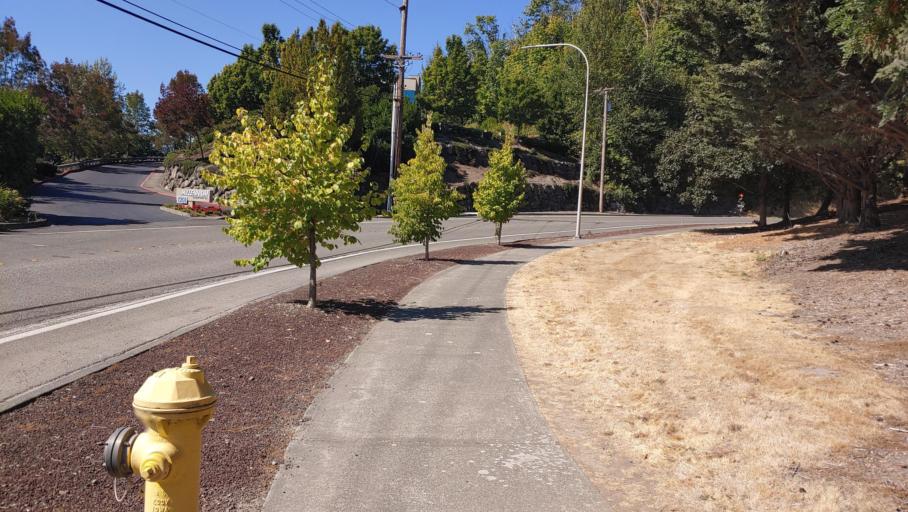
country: US
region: Washington
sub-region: King County
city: Tukwila
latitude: 47.4693
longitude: -122.2437
